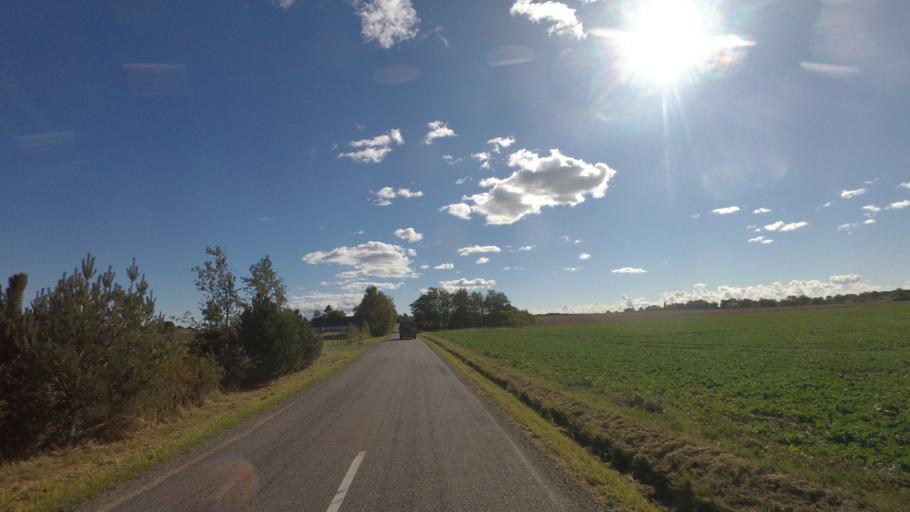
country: DK
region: Capital Region
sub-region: Bornholm Kommune
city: Akirkeby
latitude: 55.1296
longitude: 15.0243
